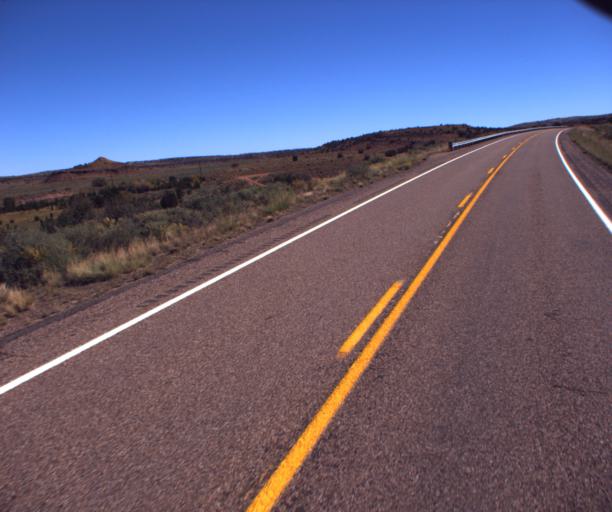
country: US
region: Arizona
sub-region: Apache County
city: Saint Johns
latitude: 34.5876
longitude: -109.5510
